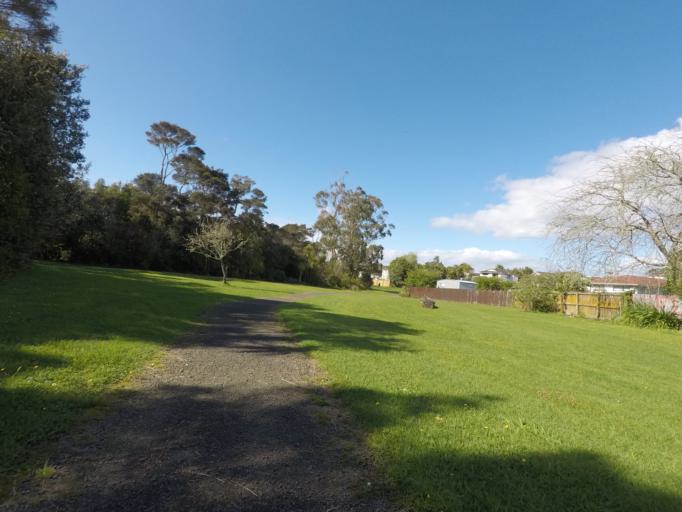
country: NZ
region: Auckland
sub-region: Auckland
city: Rosebank
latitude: -36.8594
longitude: 174.5972
